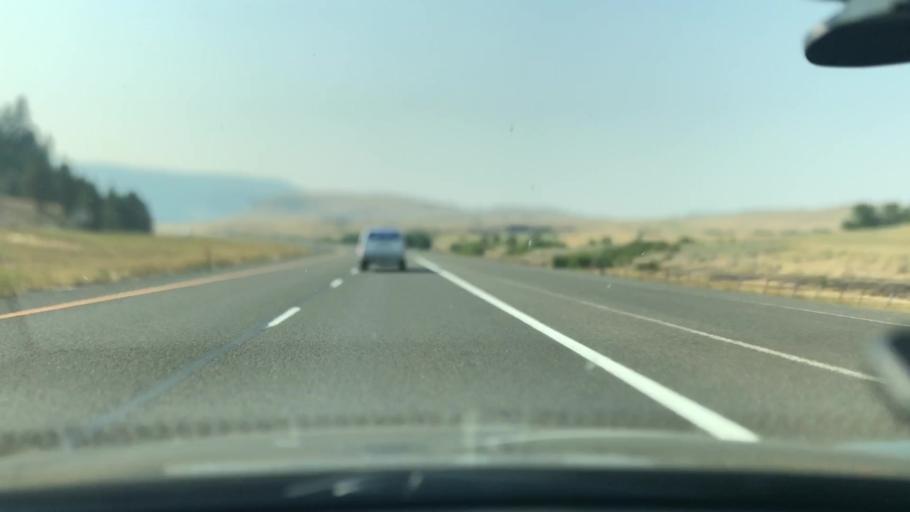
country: US
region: Oregon
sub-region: Union County
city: Union
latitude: 45.1851
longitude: -117.9891
